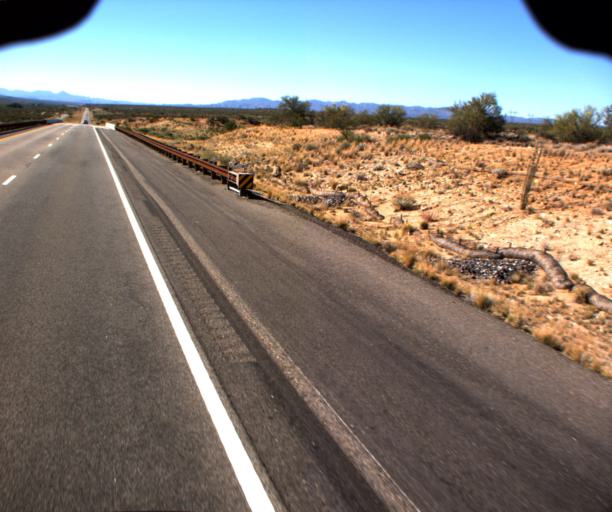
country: US
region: Arizona
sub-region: Mohave County
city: Kingman
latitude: 34.8635
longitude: -113.6425
